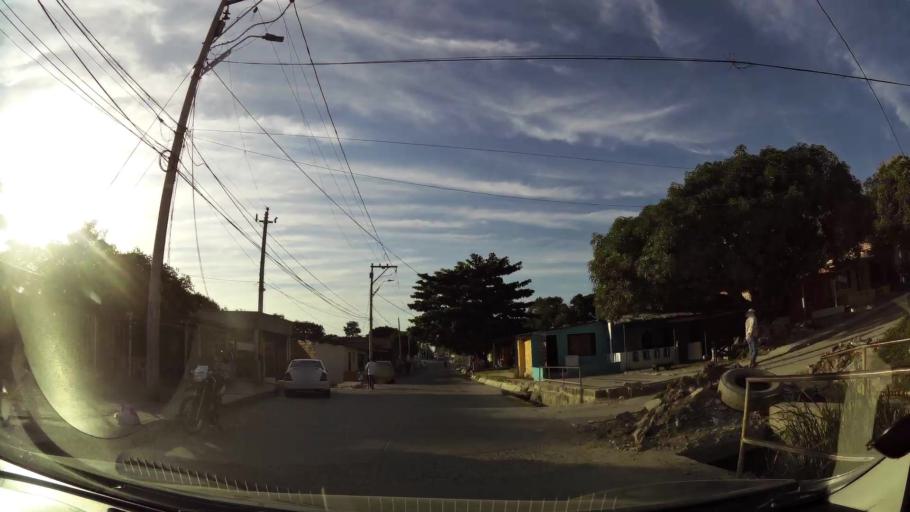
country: CO
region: Atlantico
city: Barranquilla
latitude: 10.9542
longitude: -74.8146
